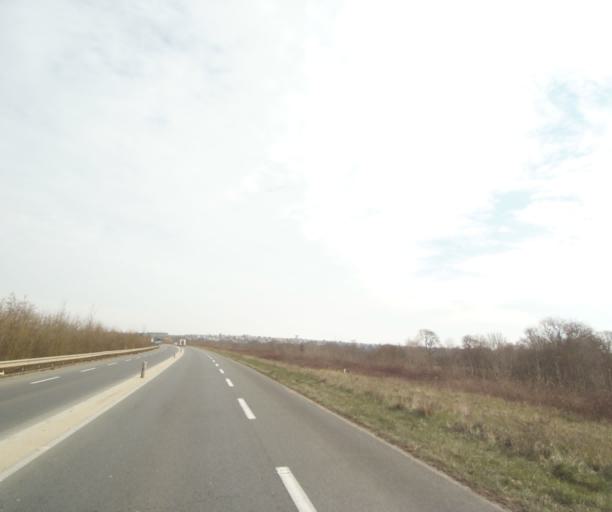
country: FR
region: Poitou-Charentes
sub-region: Departement des Deux-Sevres
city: Aiffres
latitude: 46.2954
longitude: -0.4466
